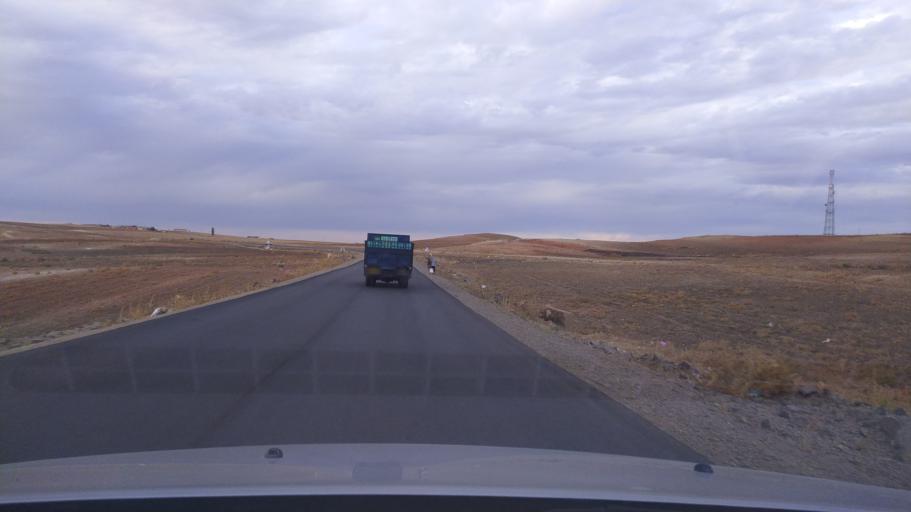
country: DZ
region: Tiaret
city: Frenda
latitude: 34.9958
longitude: 1.1280
